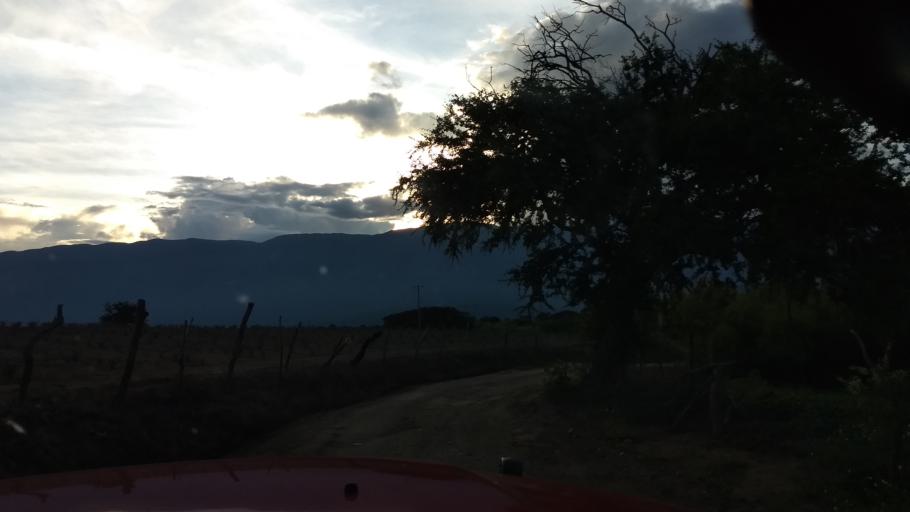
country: MX
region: Colima
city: Suchitlan
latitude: 19.4921
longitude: -103.7849
